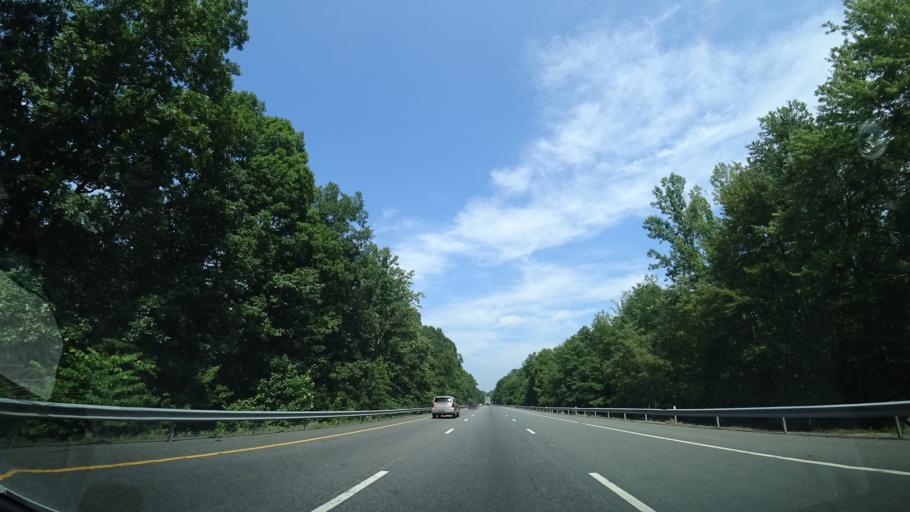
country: US
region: Virginia
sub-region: Fluvanna County
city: Lake Monticello
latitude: 37.9967
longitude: -78.3326
